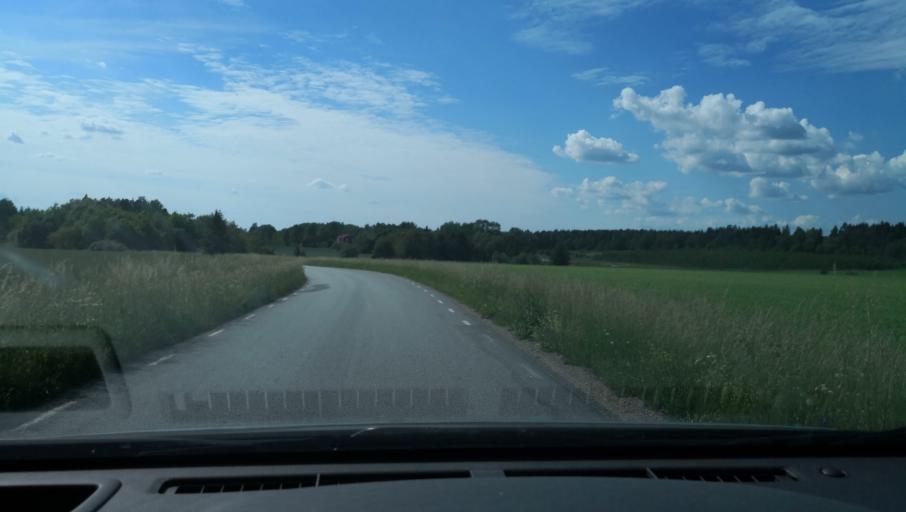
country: SE
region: Uppsala
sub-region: Enkopings Kommun
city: Orsundsbro
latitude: 59.8143
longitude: 17.3730
